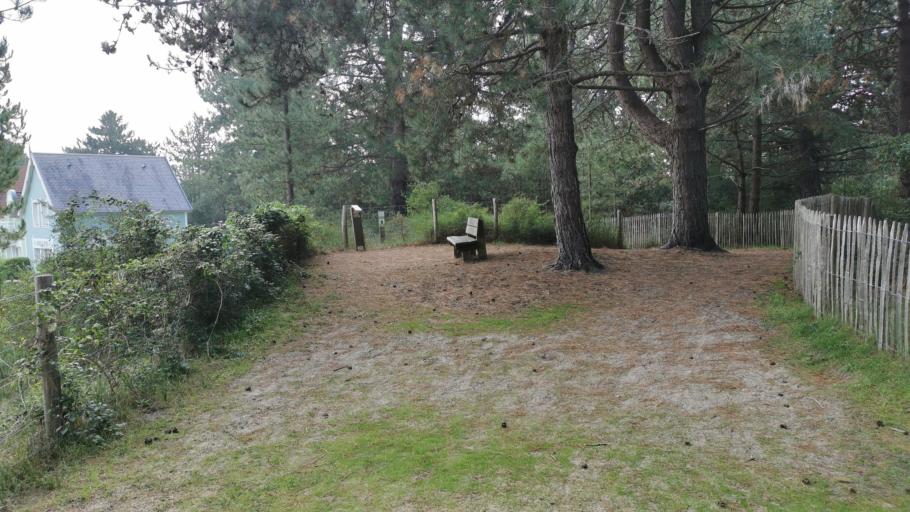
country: FR
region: Picardie
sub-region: Departement de la Somme
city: Fort-Mahon-Plage
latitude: 50.3278
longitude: 1.5646
